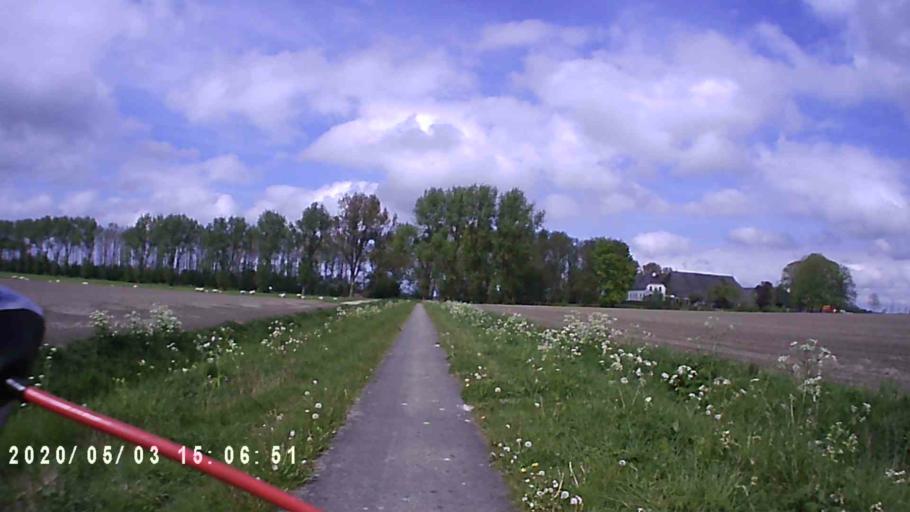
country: NL
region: Groningen
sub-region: Gemeente Zuidhorn
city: Oldehove
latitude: 53.3740
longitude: 6.4412
